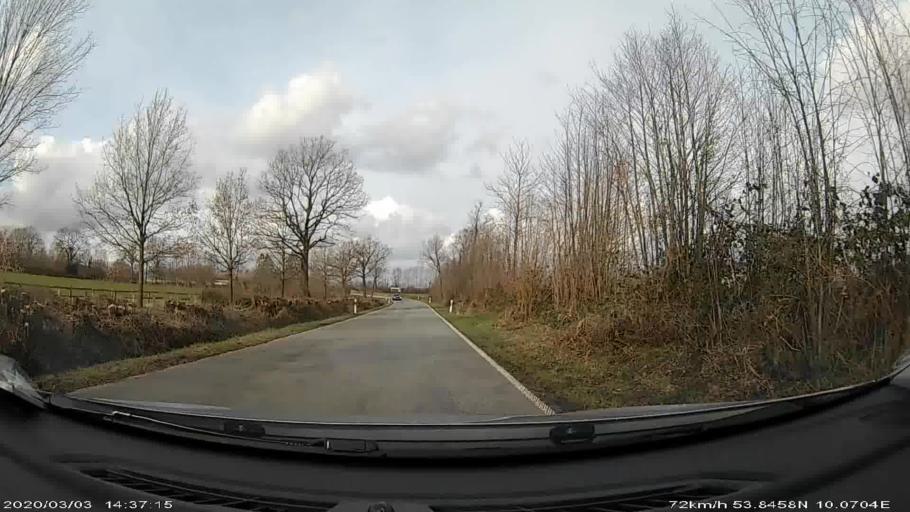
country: DE
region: Schleswig-Holstein
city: Huttblek
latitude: 53.8461
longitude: 10.0704
